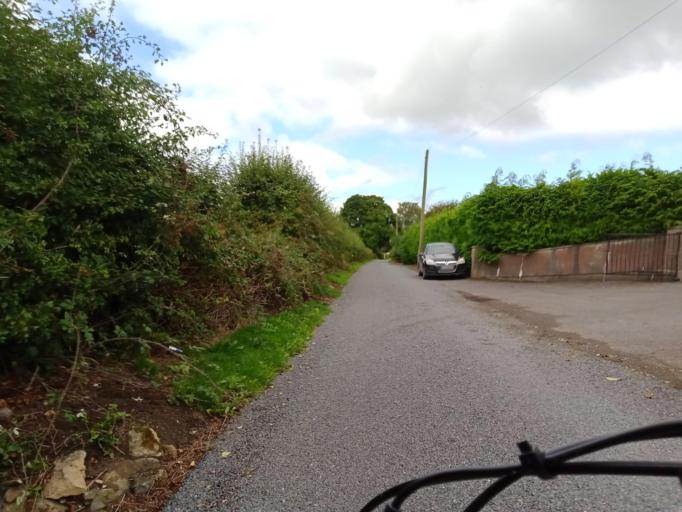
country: IE
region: Leinster
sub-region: Kilkenny
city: Callan
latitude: 52.5306
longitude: -7.2874
